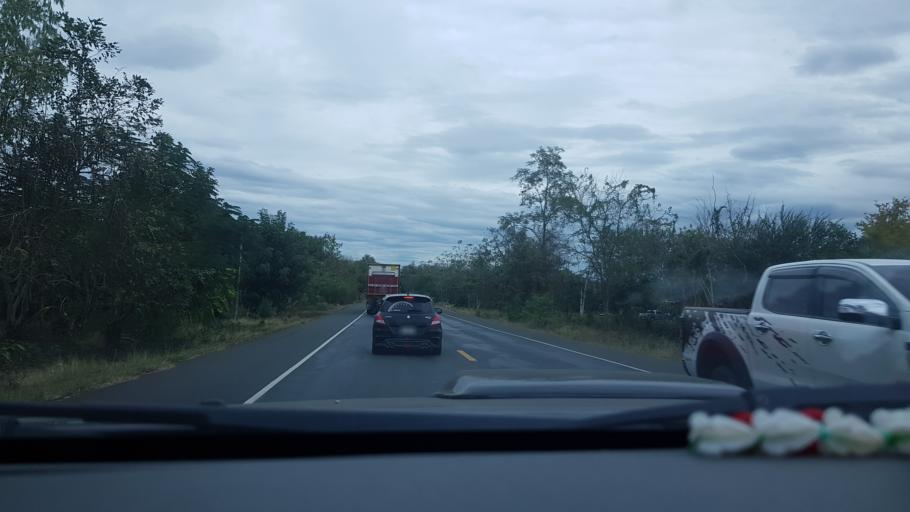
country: TH
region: Phetchabun
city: Phetchabun
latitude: 16.4806
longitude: 101.1346
